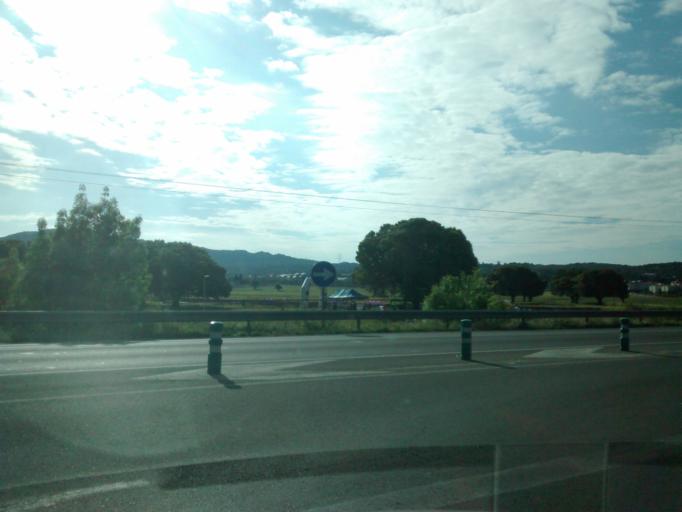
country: ES
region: Madrid
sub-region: Provincia de Madrid
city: Collado-Villalba
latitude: 40.6485
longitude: -4.0075
